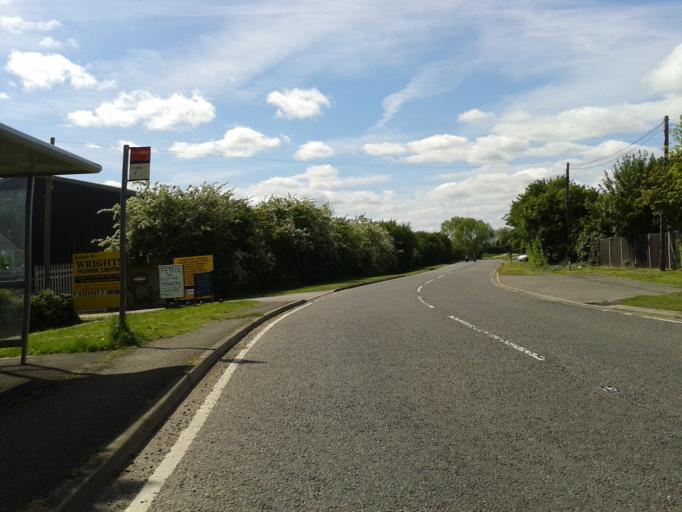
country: GB
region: England
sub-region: Cambridgeshire
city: Melbourn
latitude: 52.0992
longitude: 0.0367
